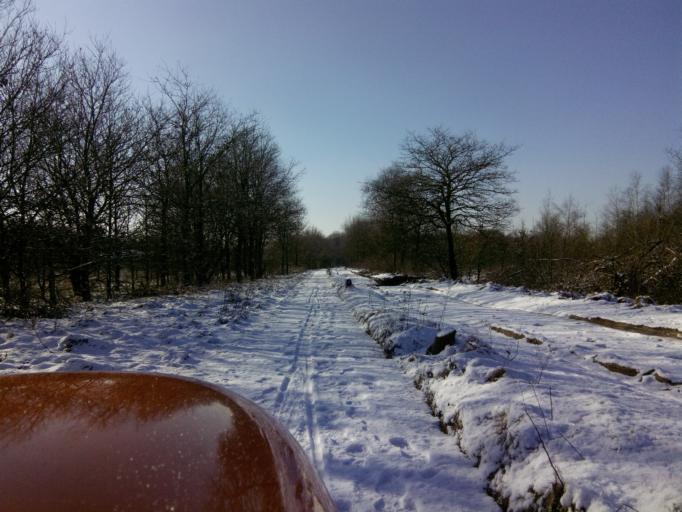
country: NL
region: Gelderland
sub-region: Gemeente Barneveld
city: Stroe
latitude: 52.1738
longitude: 5.7094
